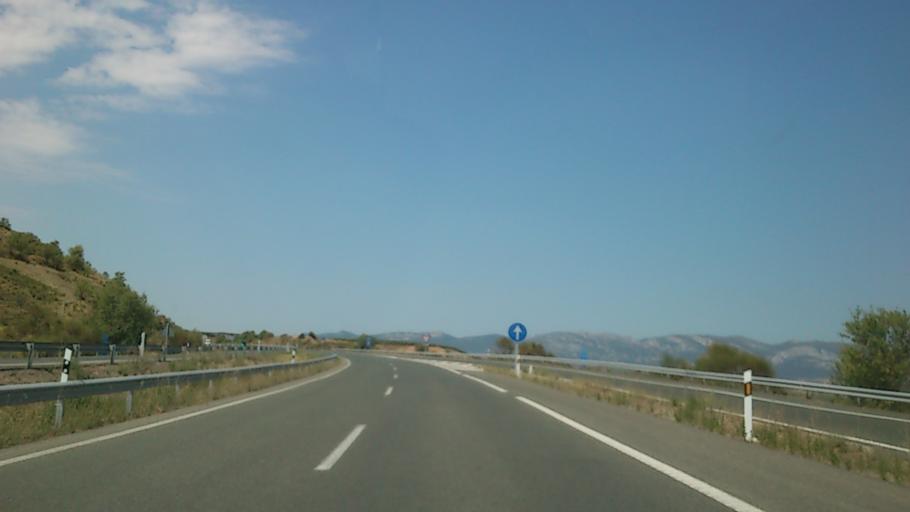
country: ES
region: La Rioja
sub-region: Provincia de La Rioja
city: Cenicero
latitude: 42.4702
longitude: -2.6465
